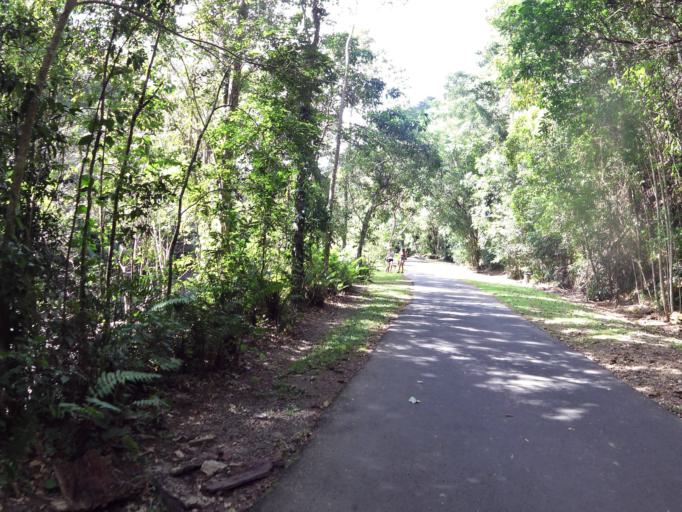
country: AU
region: Queensland
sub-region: Cairns
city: Woree
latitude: -16.9649
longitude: 145.6754
